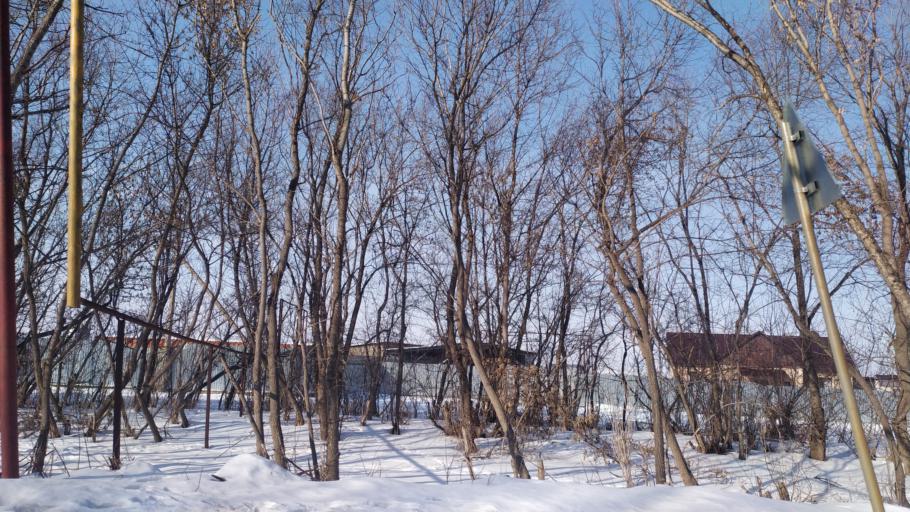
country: KZ
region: Almaty Oblysy
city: Burunday
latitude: 43.2398
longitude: 76.4220
